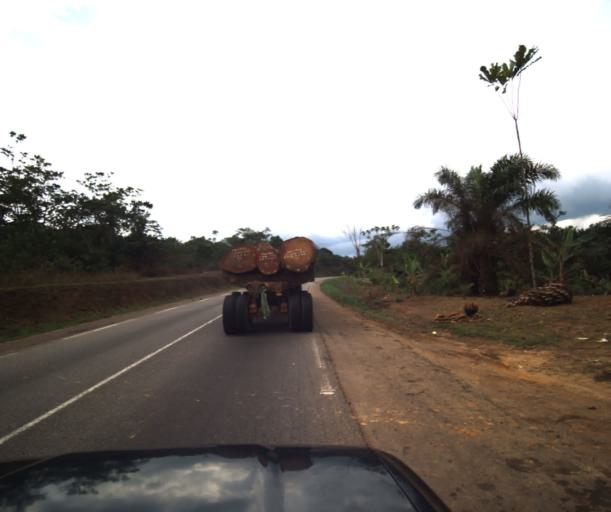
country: CM
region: Littoral
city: Edea
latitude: 3.9390
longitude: 10.0494
